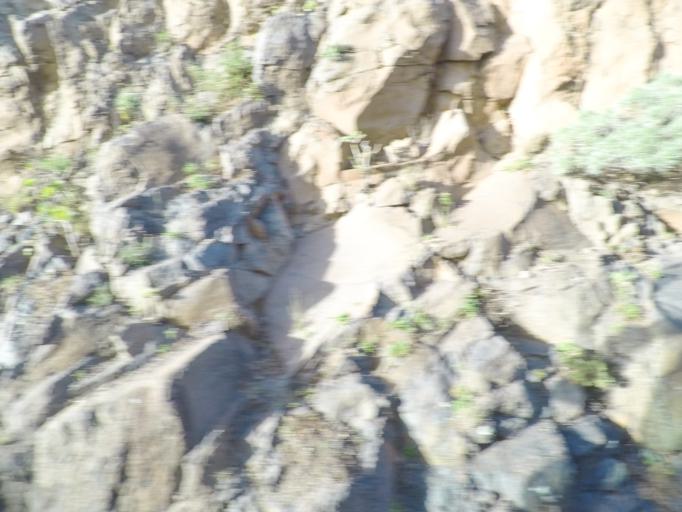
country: ES
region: Canary Islands
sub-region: Provincia de Santa Cruz de Tenerife
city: San Sebastian de la Gomera
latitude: 28.0979
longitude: -17.1778
